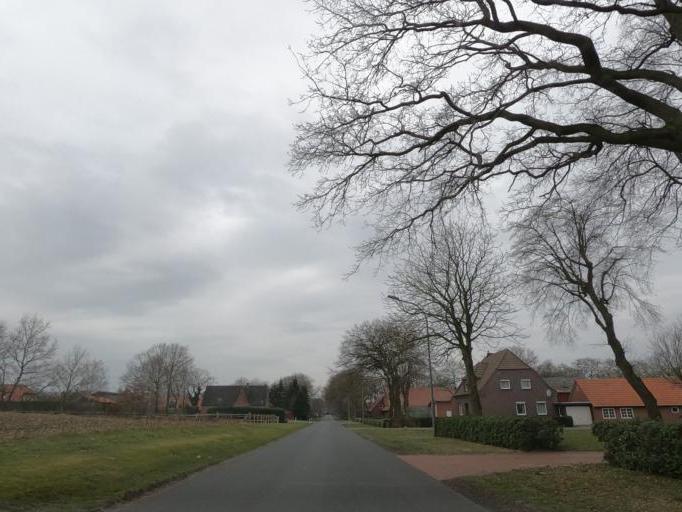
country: DE
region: Lower Saxony
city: Hilkenbrook
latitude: 52.9774
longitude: 7.7707
